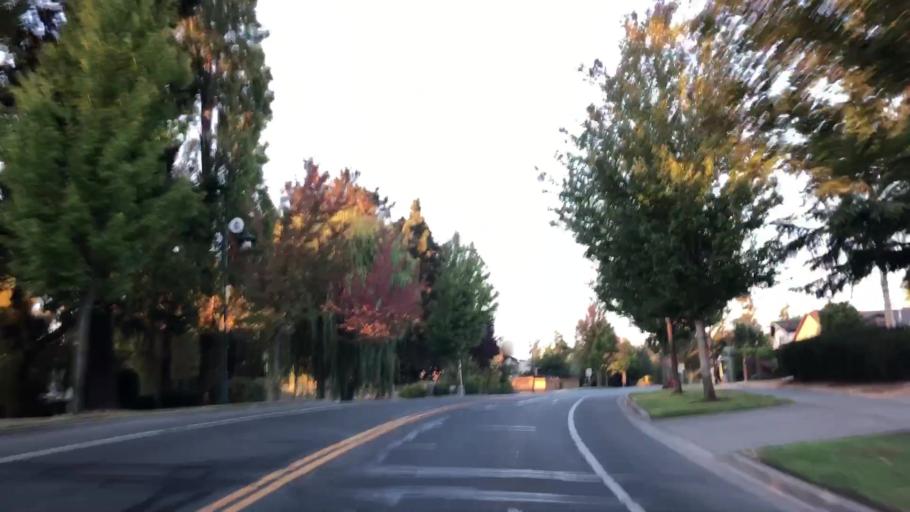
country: CA
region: British Columbia
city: Colwood
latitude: 48.4606
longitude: -123.4326
